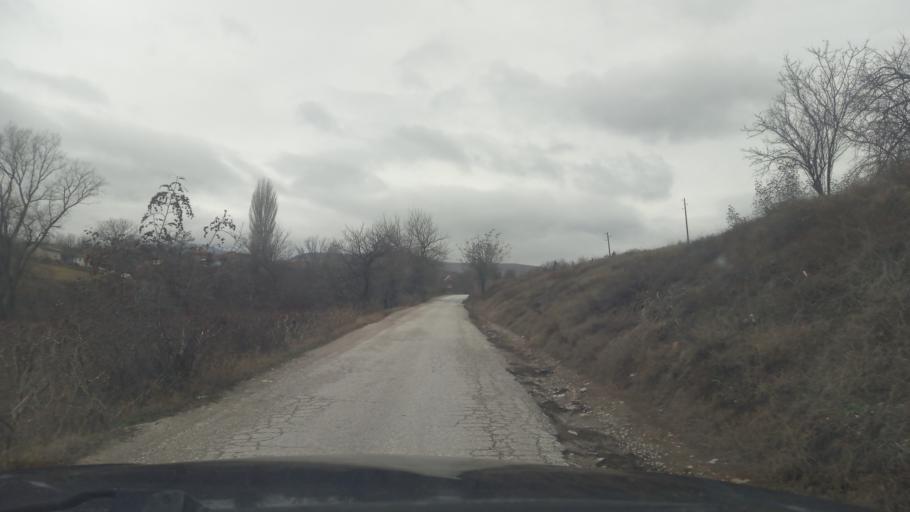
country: MK
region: Gradsko
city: Gradsko
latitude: 41.6002
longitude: 21.9029
